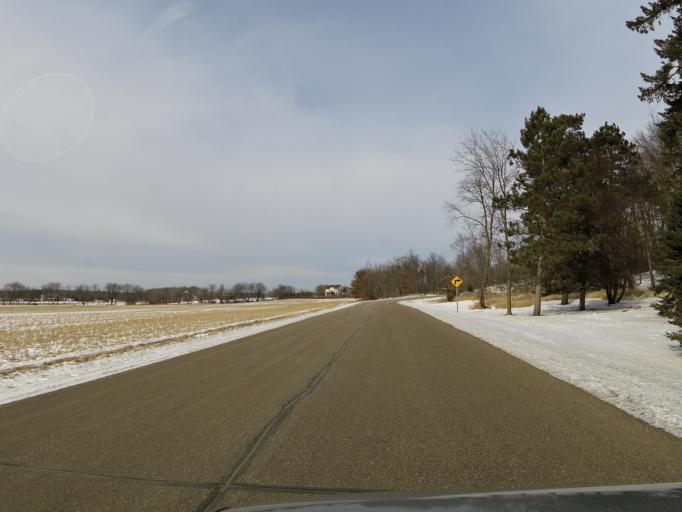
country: US
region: Minnesota
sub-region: Washington County
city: Stillwater
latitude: 45.0650
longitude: -92.7754
